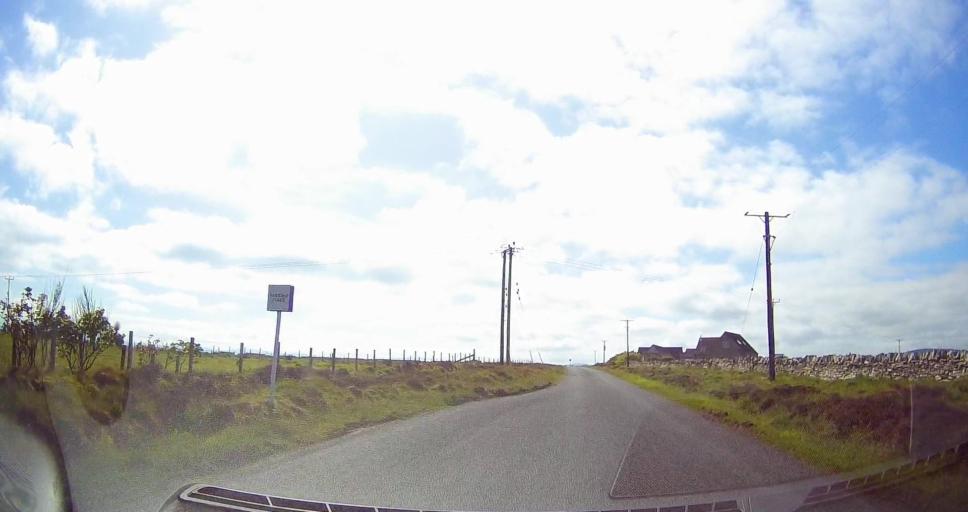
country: GB
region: Scotland
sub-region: Orkney Islands
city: Kirkwall
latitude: 58.9628
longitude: -2.9503
